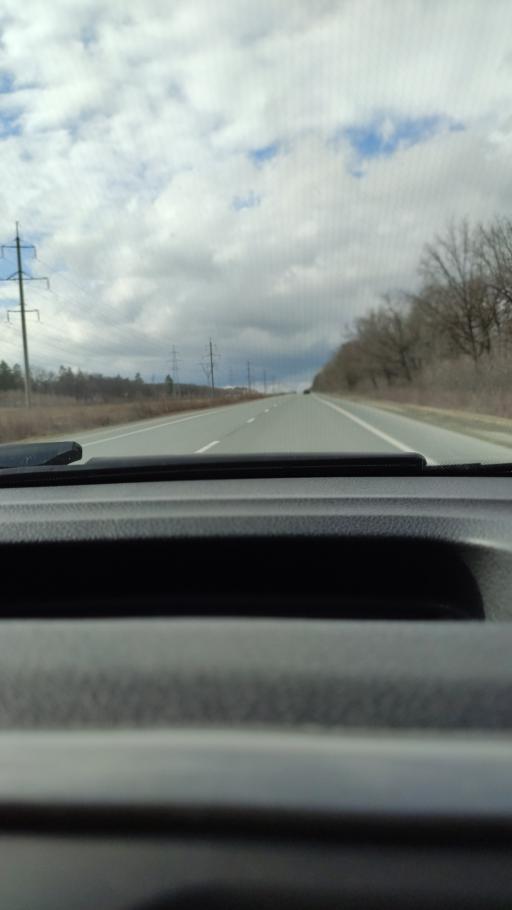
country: RU
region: Samara
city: Bogatyr'
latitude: 53.4985
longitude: 49.9568
